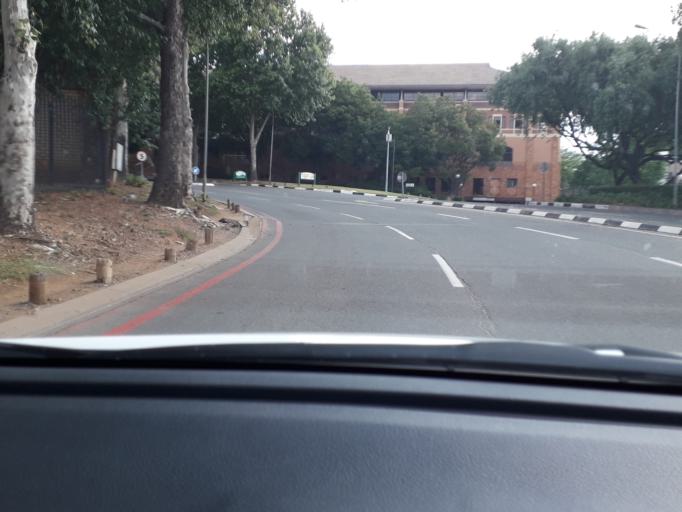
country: ZA
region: Gauteng
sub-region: City of Johannesburg Metropolitan Municipality
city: Johannesburg
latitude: -26.1804
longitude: 28.1086
